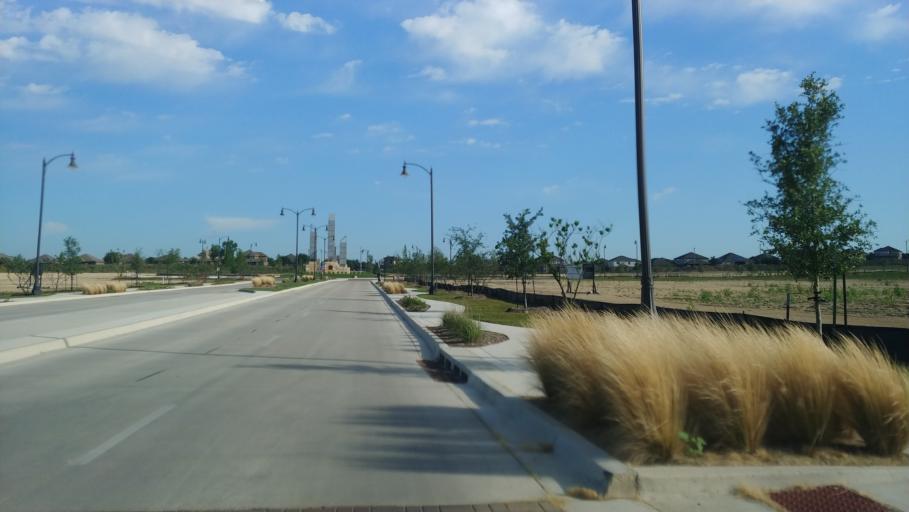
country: US
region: Texas
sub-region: Bexar County
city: Live Oak
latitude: 29.5641
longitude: -98.3422
